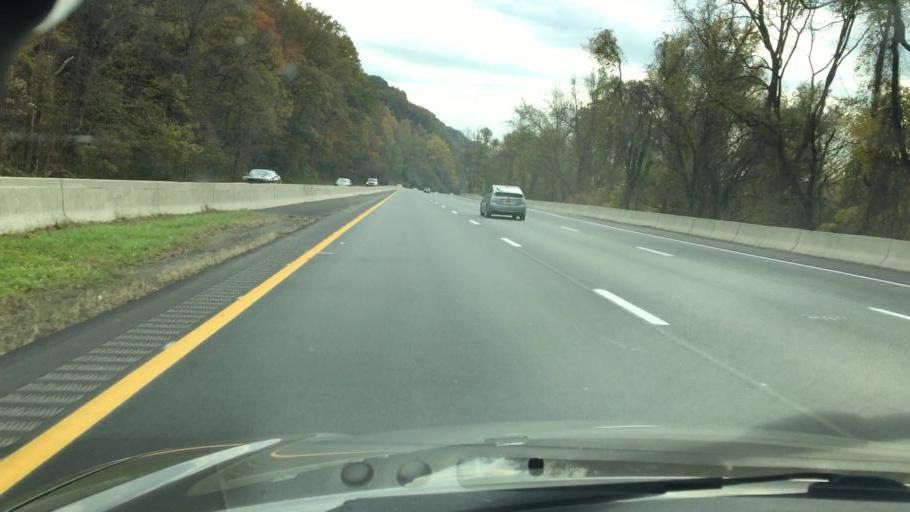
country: US
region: Pennsylvania
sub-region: Monroe County
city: East Stroudsburg
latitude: 40.9509
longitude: -75.1132
